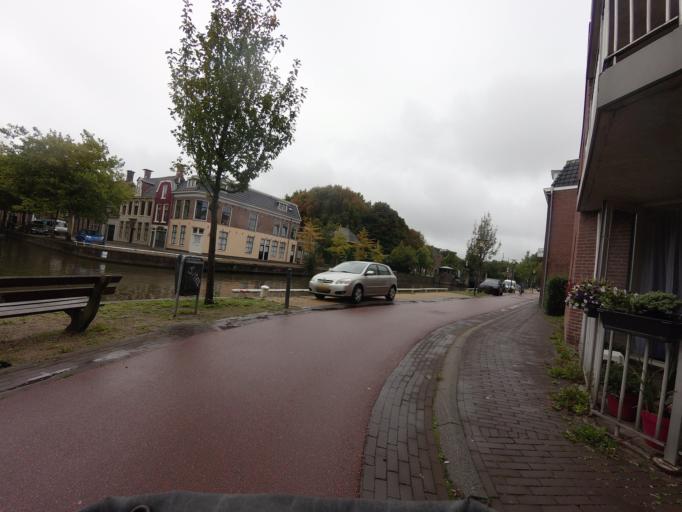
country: NL
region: Friesland
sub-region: Gemeente Leeuwarden
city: Bilgaard
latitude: 53.2072
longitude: 5.7979
